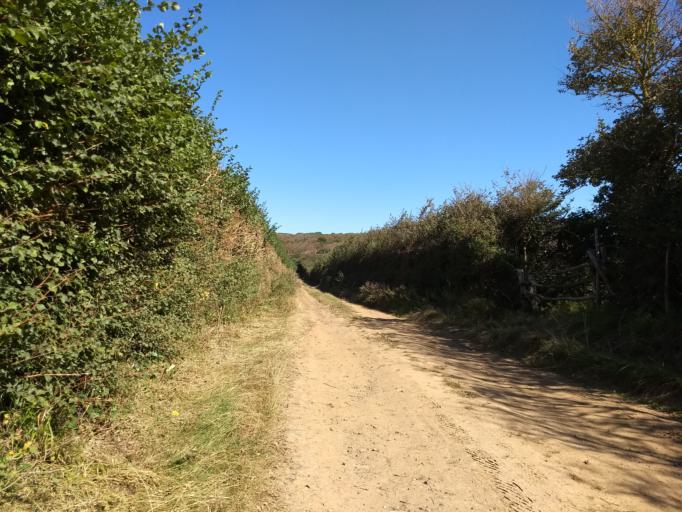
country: GB
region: England
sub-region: Isle of Wight
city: Shalfleet
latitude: 50.6492
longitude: -1.4300
